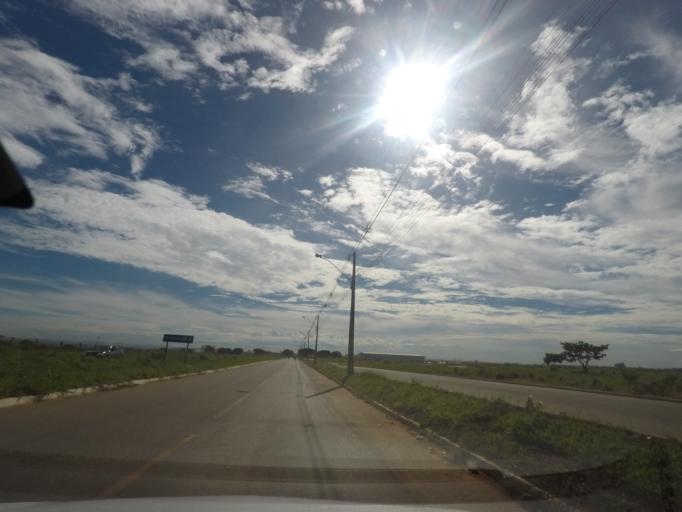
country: BR
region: Goias
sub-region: Aparecida De Goiania
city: Aparecida de Goiania
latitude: -16.8094
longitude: -49.2765
